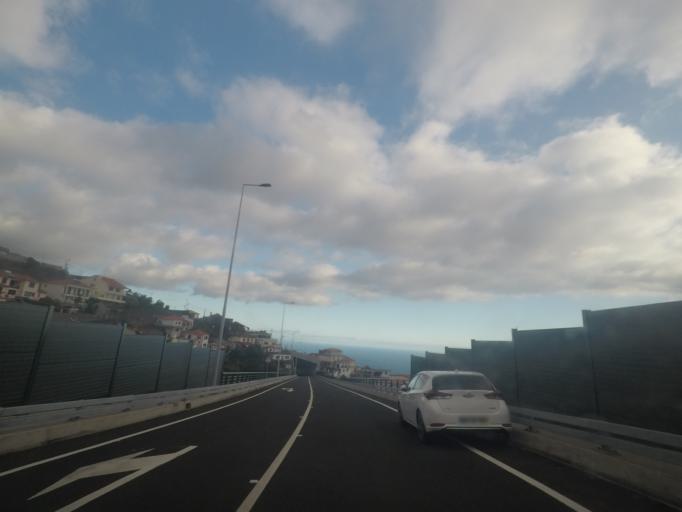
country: PT
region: Madeira
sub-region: Funchal
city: Nossa Senhora do Monte
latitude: 32.6772
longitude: -16.9401
